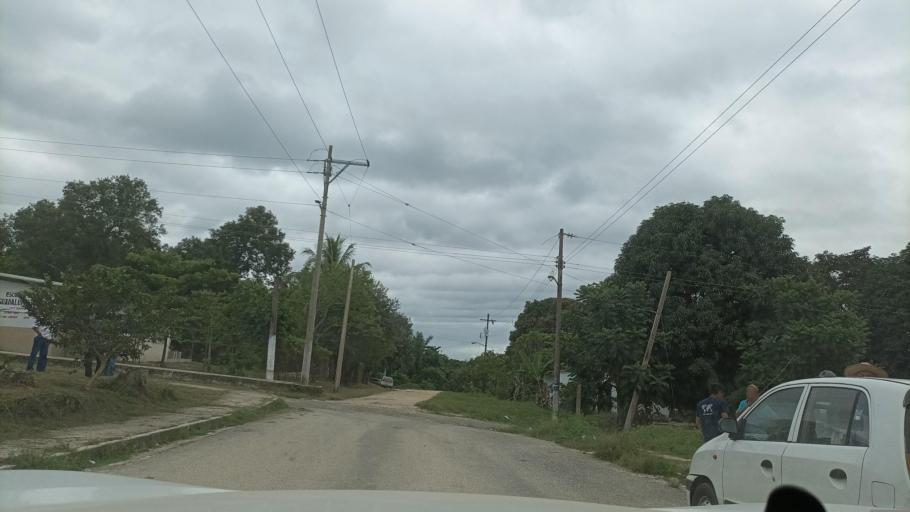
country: MX
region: Veracruz
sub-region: Cosoleacaque
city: Coacotla
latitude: 17.9444
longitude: -94.7072
